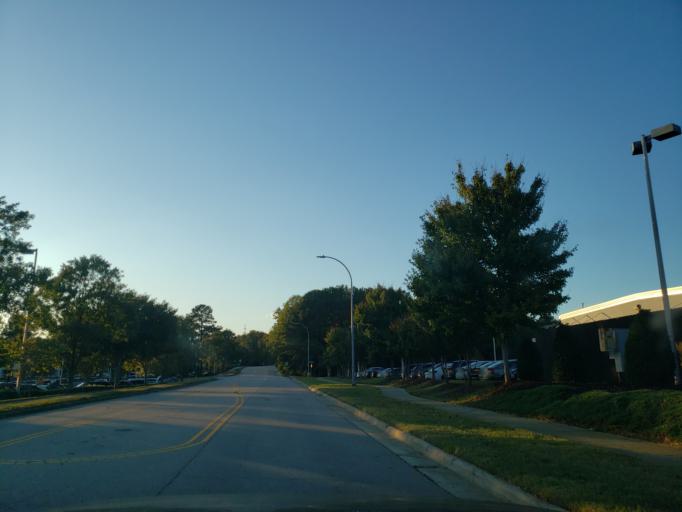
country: US
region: North Carolina
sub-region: Wake County
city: Apex
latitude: 35.7400
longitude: -78.8147
